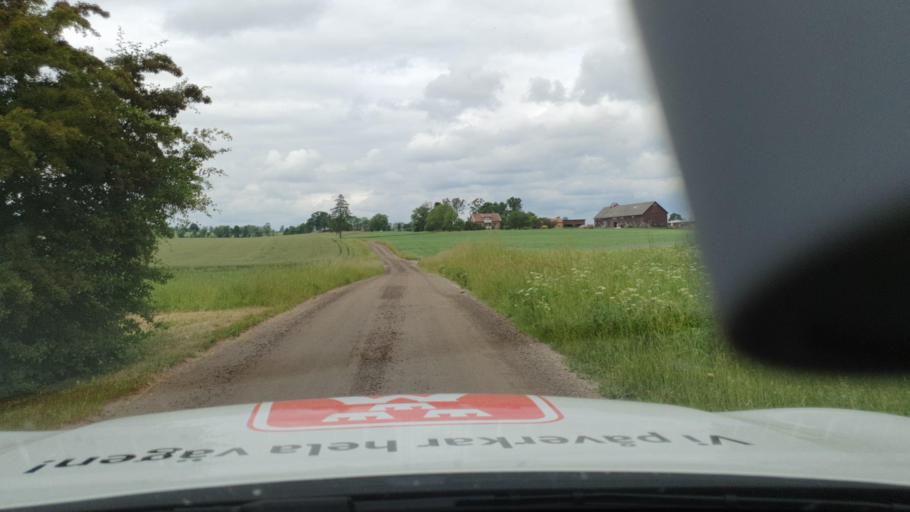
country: SE
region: Vaestra Goetaland
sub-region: Hjo Kommun
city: Hjo
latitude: 58.1888
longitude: 14.1759
